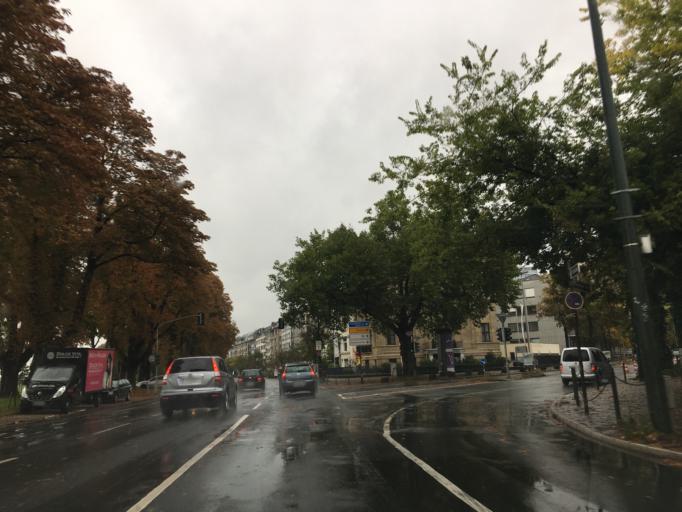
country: DE
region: North Rhine-Westphalia
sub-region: Regierungsbezirk Dusseldorf
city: Dusseldorf
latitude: 51.2415
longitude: 6.7709
